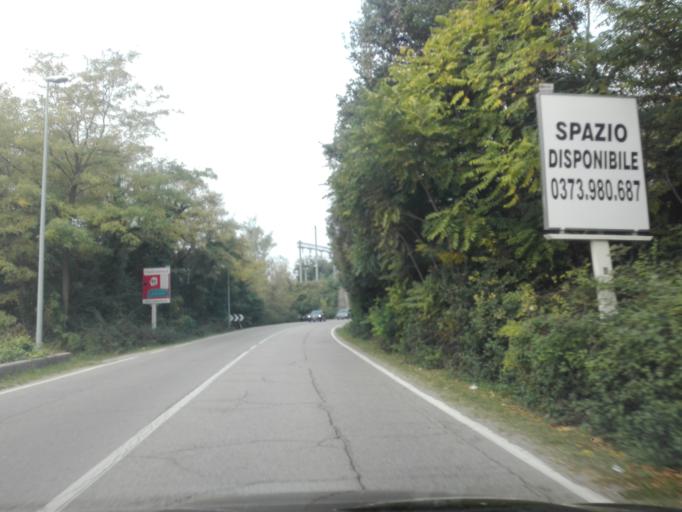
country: IT
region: Veneto
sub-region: Provincia di Verona
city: Cavalcaselle
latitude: 45.4409
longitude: 10.7094
